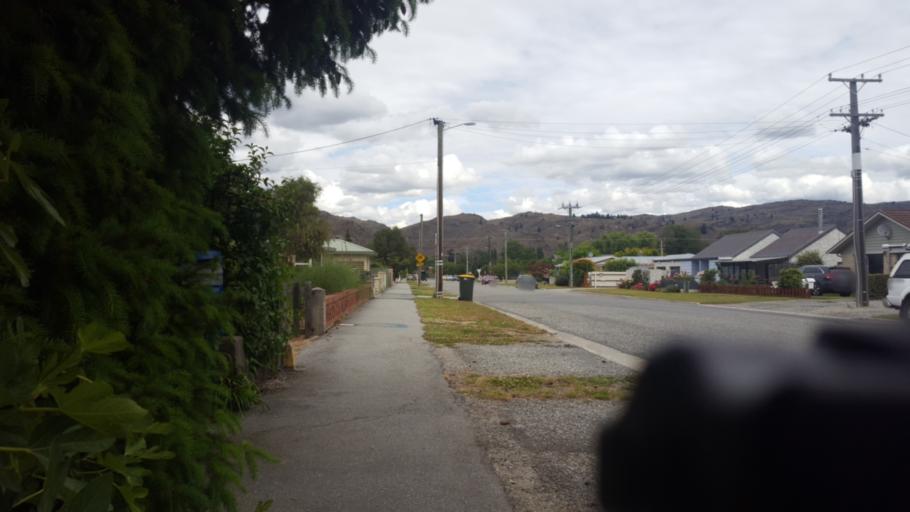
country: NZ
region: Otago
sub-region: Queenstown-Lakes District
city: Wanaka
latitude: -45.2532
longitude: 169.3882
